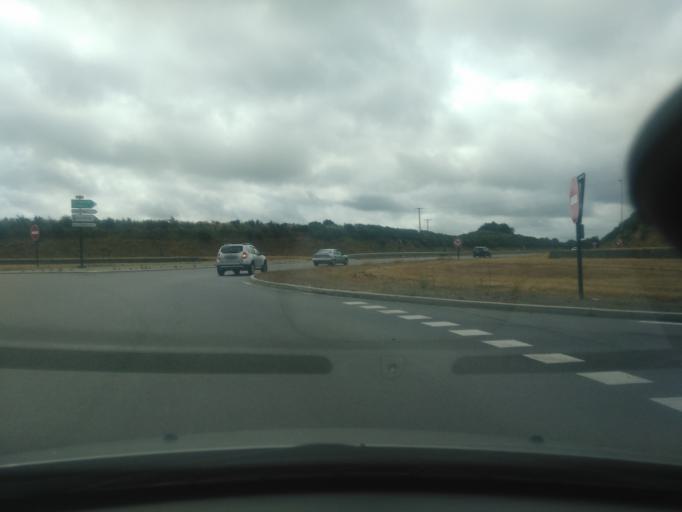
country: FR
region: Brittany
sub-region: Departement des Cotes-d'Armor
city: Ploufragan
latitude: 48.4783
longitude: -2.7687
